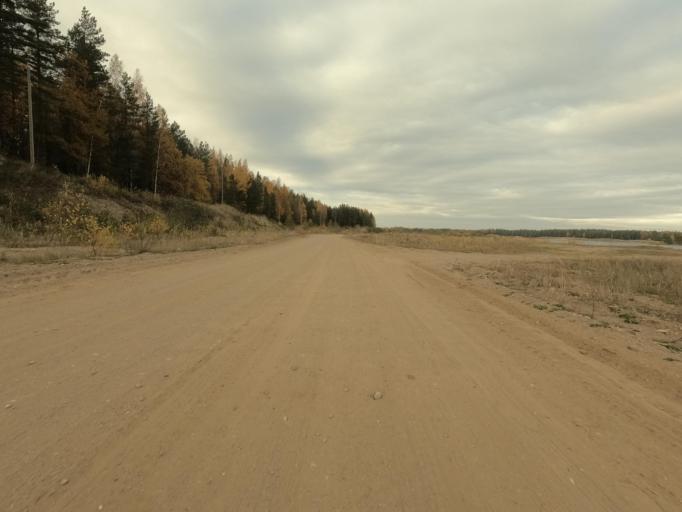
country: RU
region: Leningrad
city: Priladozhskiy
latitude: 59.7012
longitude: 31.3628
